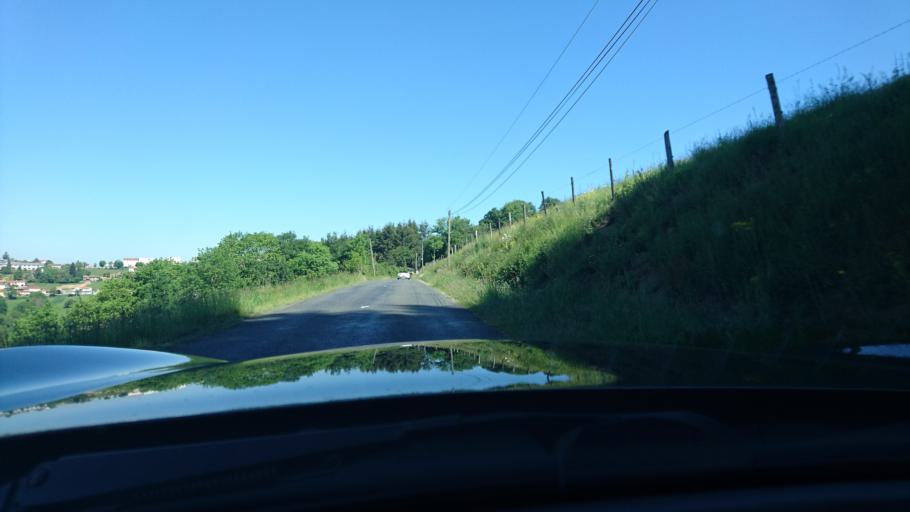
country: FR
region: Rhone-Alpes
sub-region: Departement de la Loire
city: Violay
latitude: 45.8450
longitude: 4.3644
